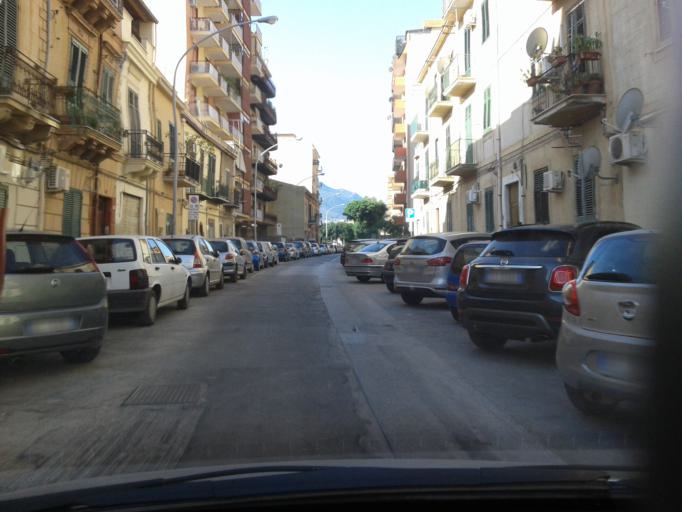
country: IT
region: Sicily
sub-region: Palermo
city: Palermo
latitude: 38.0999
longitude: 13.3384
